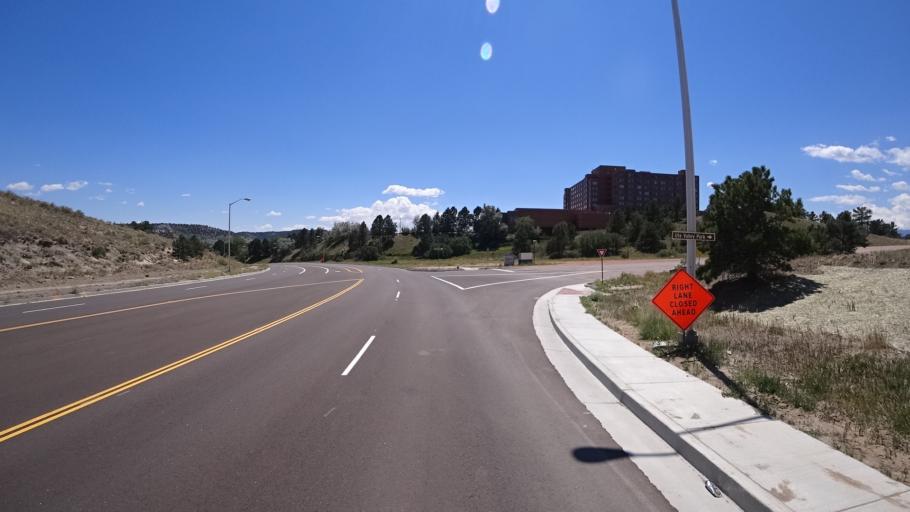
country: US
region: Colorado
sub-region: El Paso County
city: Colorado Springs
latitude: 38.9151
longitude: -104.8307
